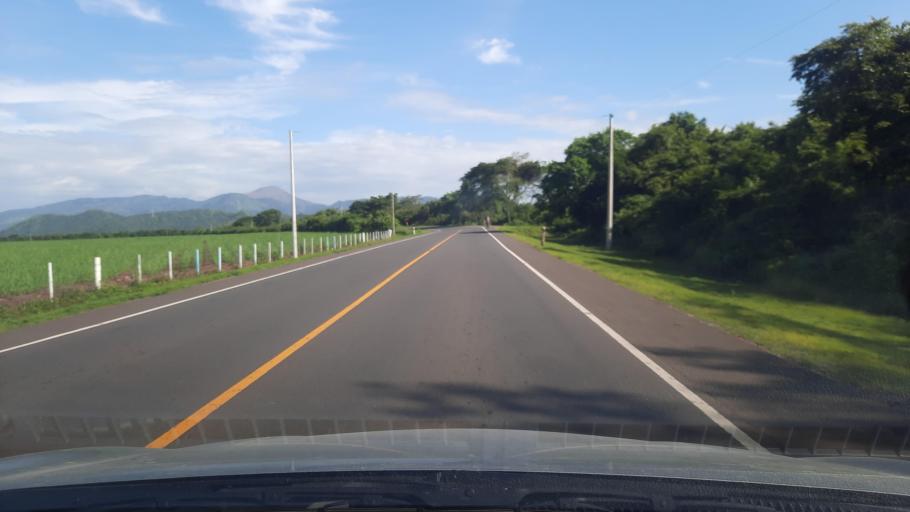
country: NI
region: Leon
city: Telica
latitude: 12.7286
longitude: -86.8803
